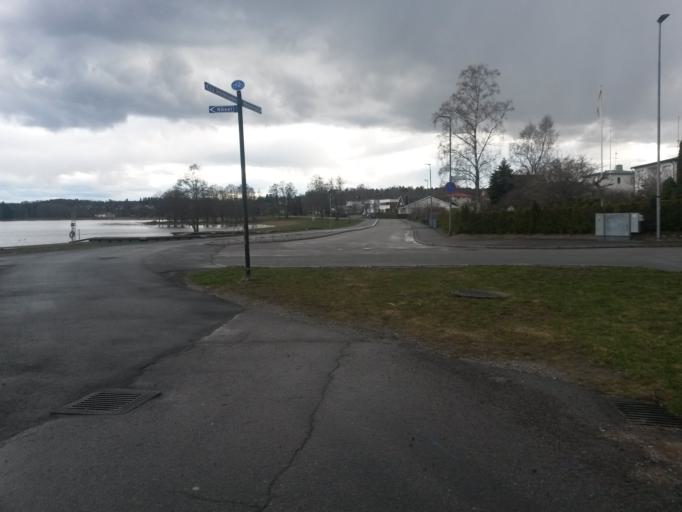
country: SE
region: OErebro
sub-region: Karlskoga Kommun
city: Karlskoga
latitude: 59.3206
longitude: 14.5227
